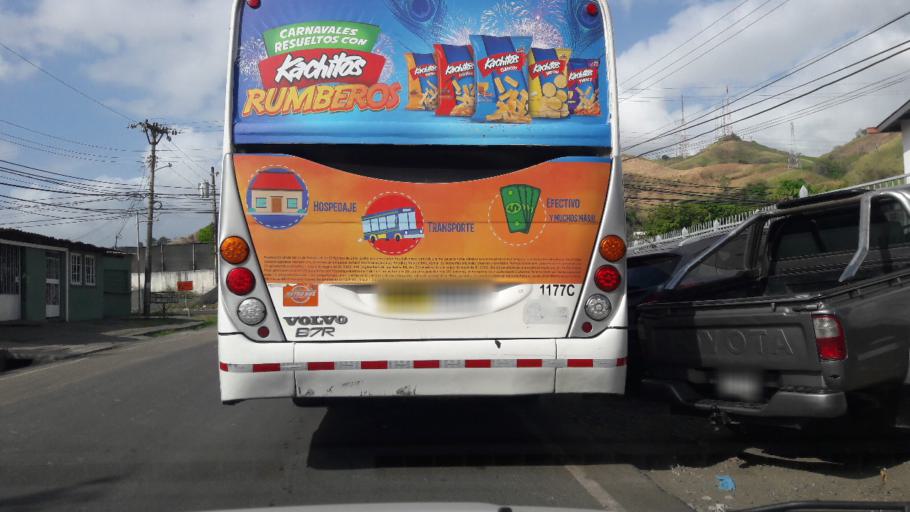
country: PA
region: Panama
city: San Miguelito
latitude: 9.0496
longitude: -79.5100
